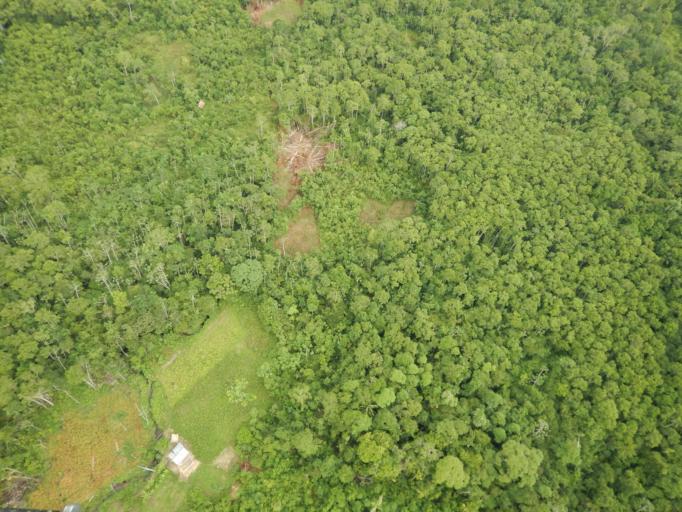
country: BO
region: Cochabamba
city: Chimore
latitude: -16.9589
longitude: -64.9942
